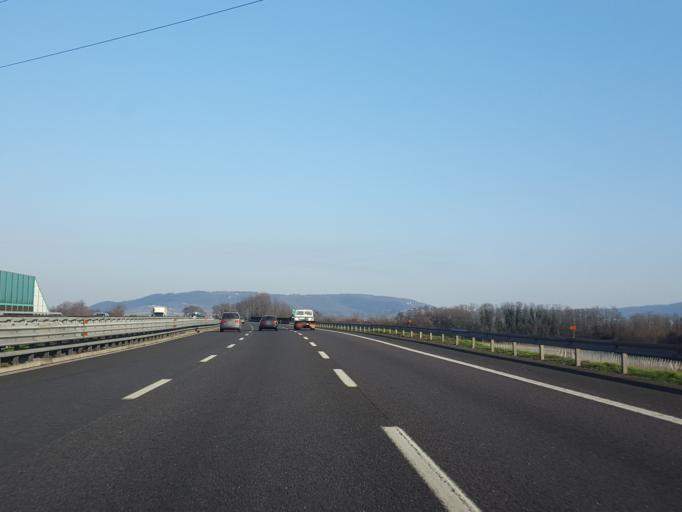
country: IT
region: Veneto
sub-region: Provincia di Vicenza
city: Montebello Vicentino
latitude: 45.4549
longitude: 11.3947
